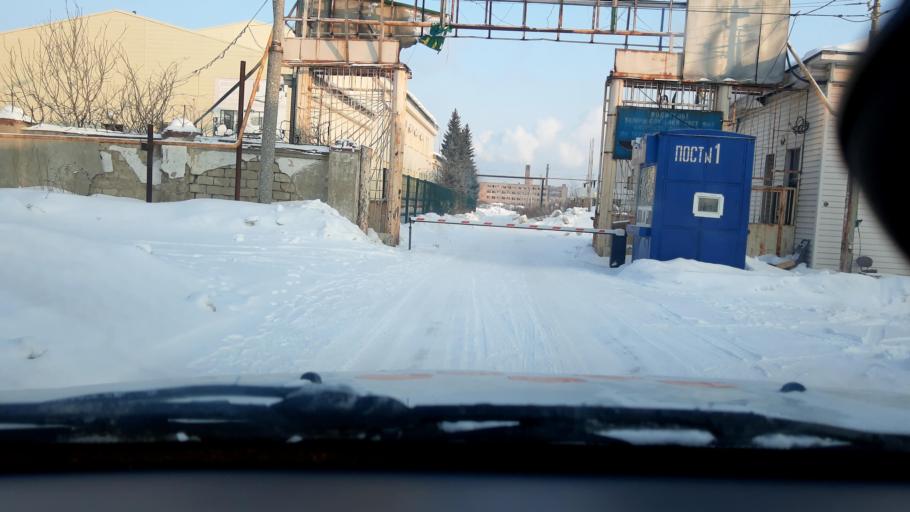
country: RU
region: Bashkortostan
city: Ufa
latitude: 54.8381
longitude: 56.0978
